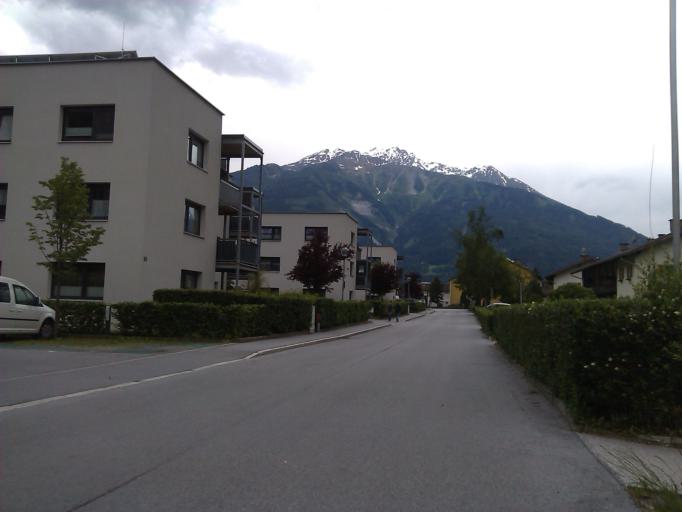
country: AT
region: Tyrol
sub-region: Politischer Bezirk Landeck
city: Zams
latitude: 47.1619
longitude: 10.5896
